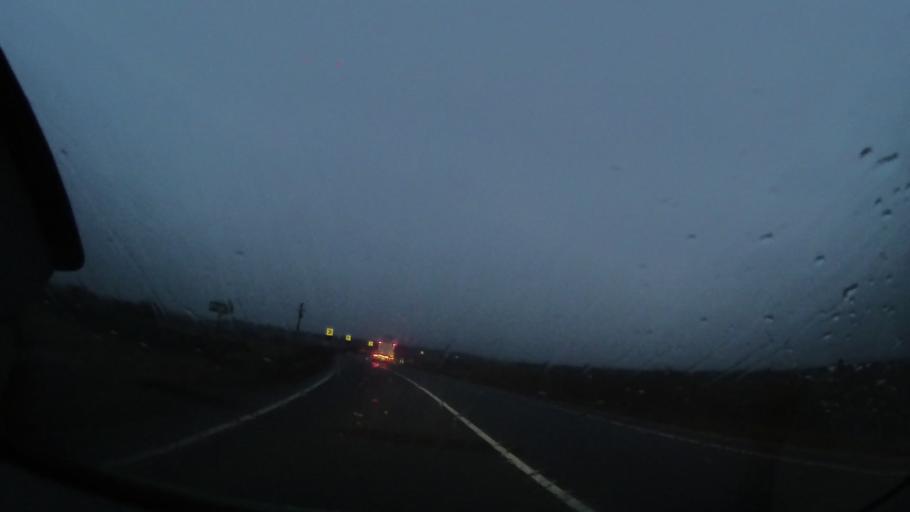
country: RO
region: Harghita
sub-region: Comuna Ditrau
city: Ditrau
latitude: 46.8177
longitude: 25.4923
